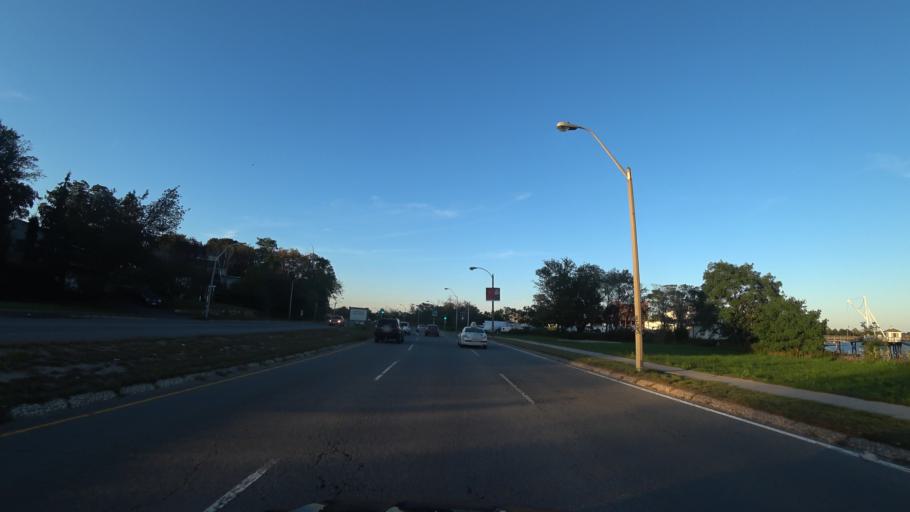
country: US
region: Massachusetts
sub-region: Suffolk County
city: South Boston
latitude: 42.3081
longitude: -71.0458
